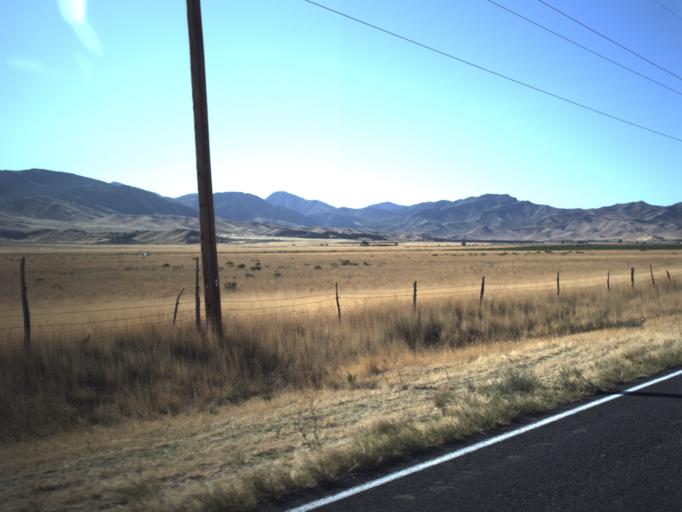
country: US
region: Utah
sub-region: Millard County
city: Delta
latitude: 39.4192
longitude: -112.3287
